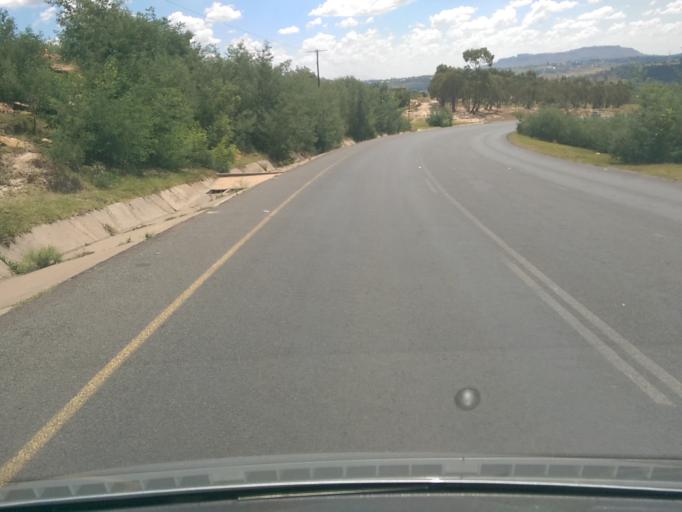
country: LS
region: Maseru
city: Maseru
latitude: -29.4078
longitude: 27.5766
